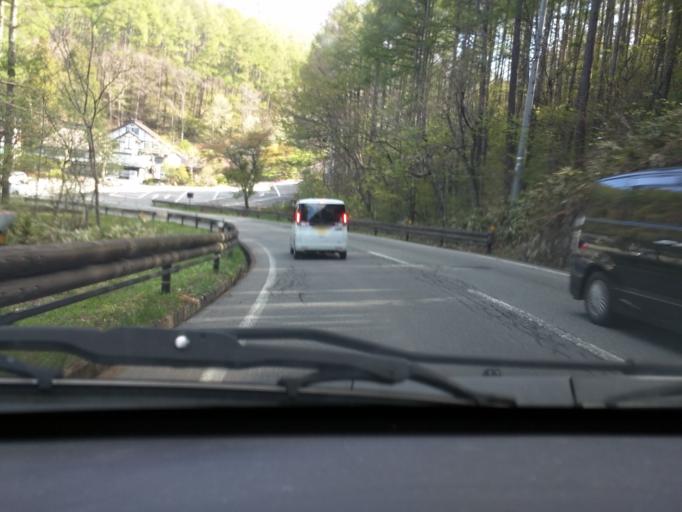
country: JP
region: Nagano
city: Nagano-shi
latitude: 36.7146
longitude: 138.1149
